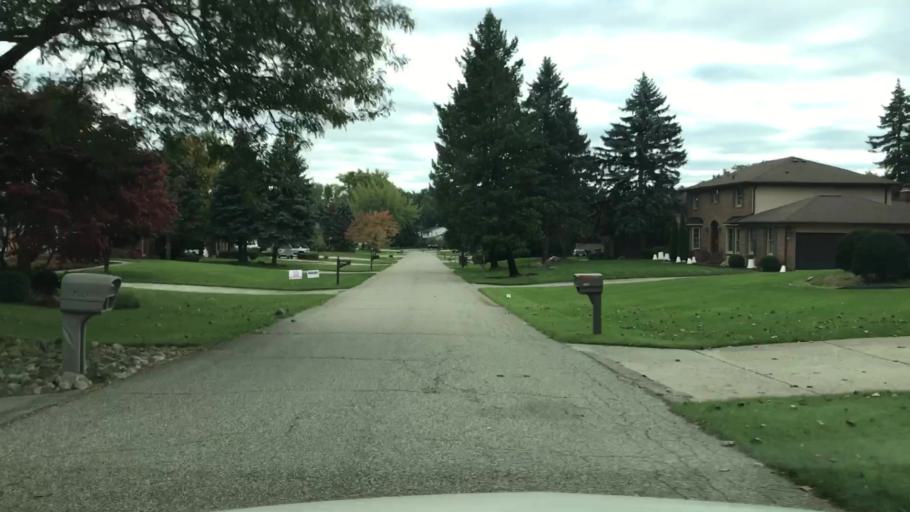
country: US
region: Michigan
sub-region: Macomb County
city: Shelby
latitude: 42.7037
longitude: -83.0724
